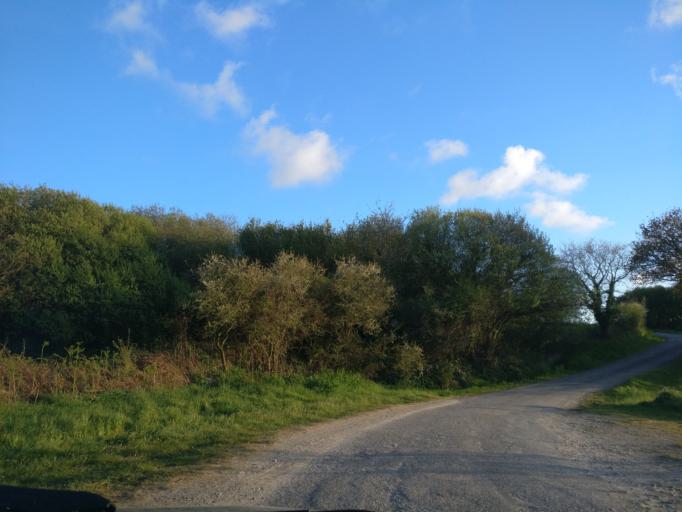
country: FR
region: Brittany
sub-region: Departement du Finistere
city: Lampaul-Plouarzel
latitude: 48.4708
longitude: -4.7467
